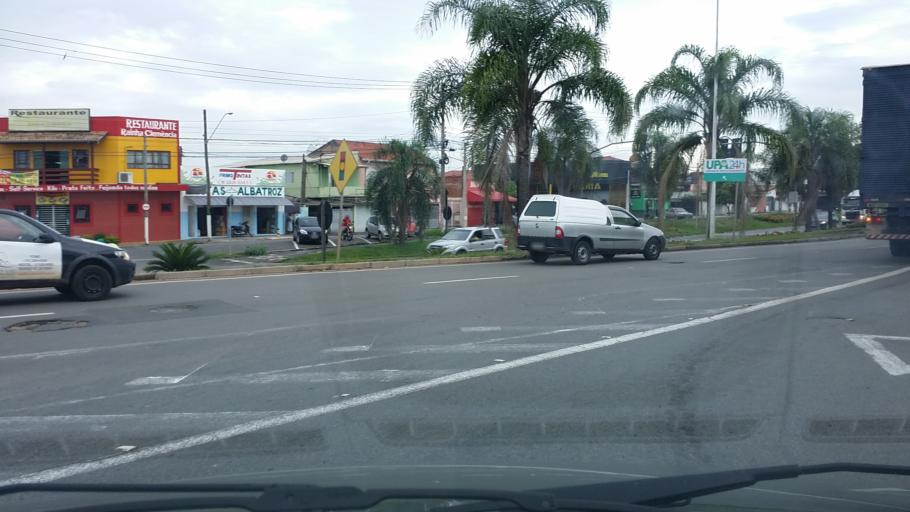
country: BR
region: Sao Paulo
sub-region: Indaiatuba
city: Indaiatuba
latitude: -23.1230
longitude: -47.2250
